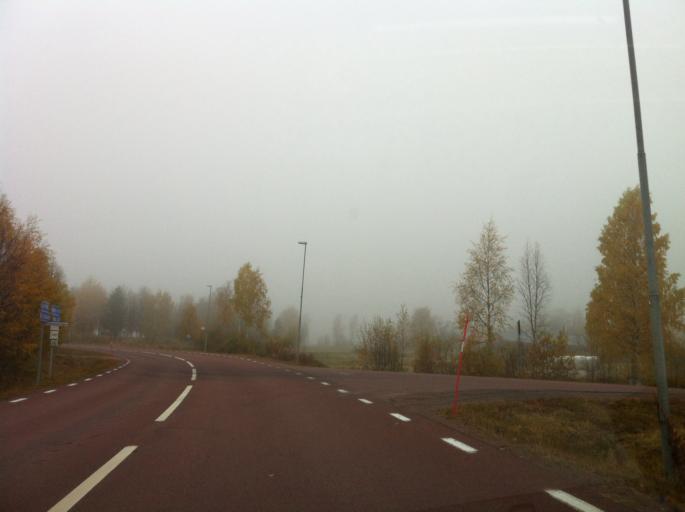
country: NO
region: Hedmark
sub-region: Trysil
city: Innbygda
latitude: 61.6891
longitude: 13.1620
